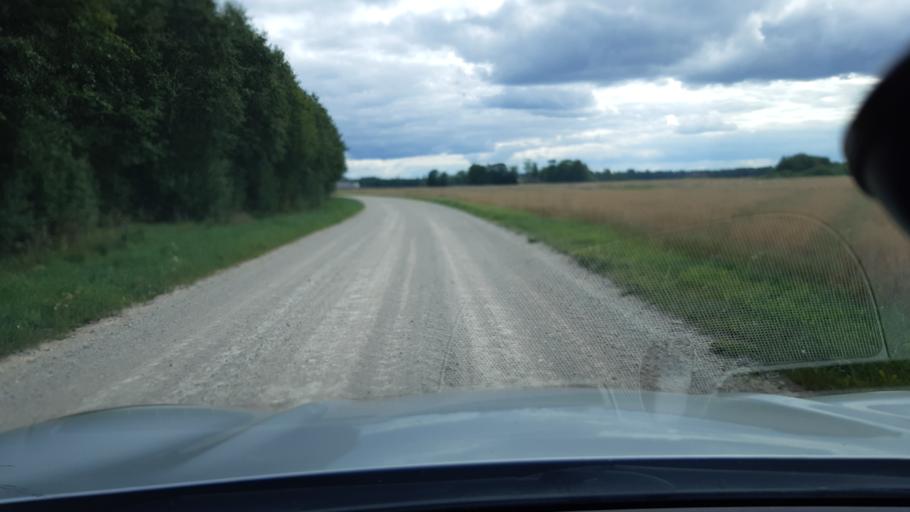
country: EE
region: Paernumaa
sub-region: Vaendra vald (alev)
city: Vandra
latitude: 58.7833
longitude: 25.0410
